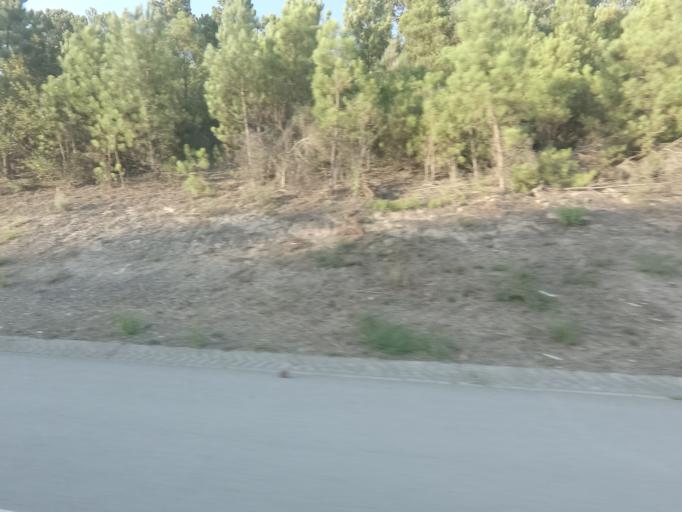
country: PT
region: Vila Real
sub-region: Vila Real
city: Vila Real
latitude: 41.3136
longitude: -7.6911
